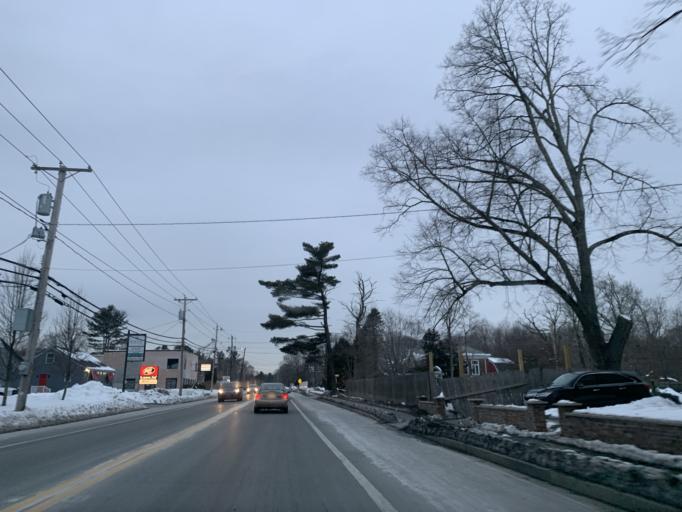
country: US
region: Massachusetts
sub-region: Norfolk County
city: Stoughton
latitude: 42.1121
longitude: -71.0744
